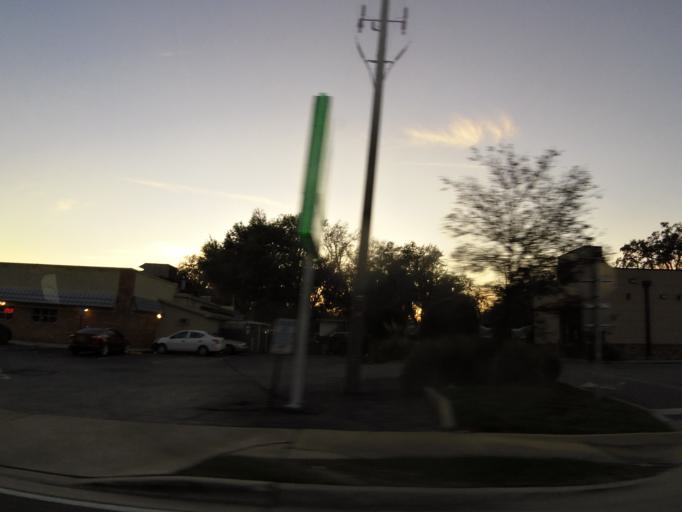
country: US
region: Florida
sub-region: Clay County
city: Orange Park
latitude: 30.1725
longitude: -81.7015
